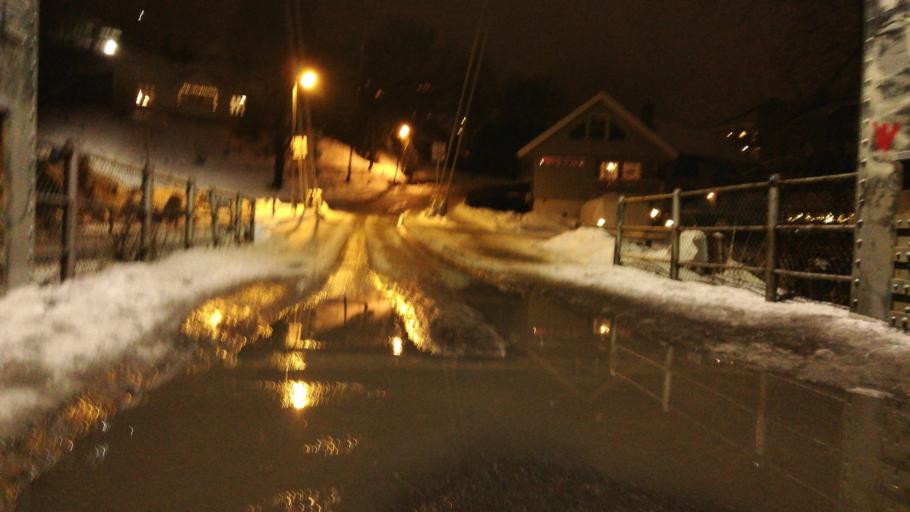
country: NO
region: Buskerud
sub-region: Kongsberg
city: Kongsberg
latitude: 59.6627
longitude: 9.6516
